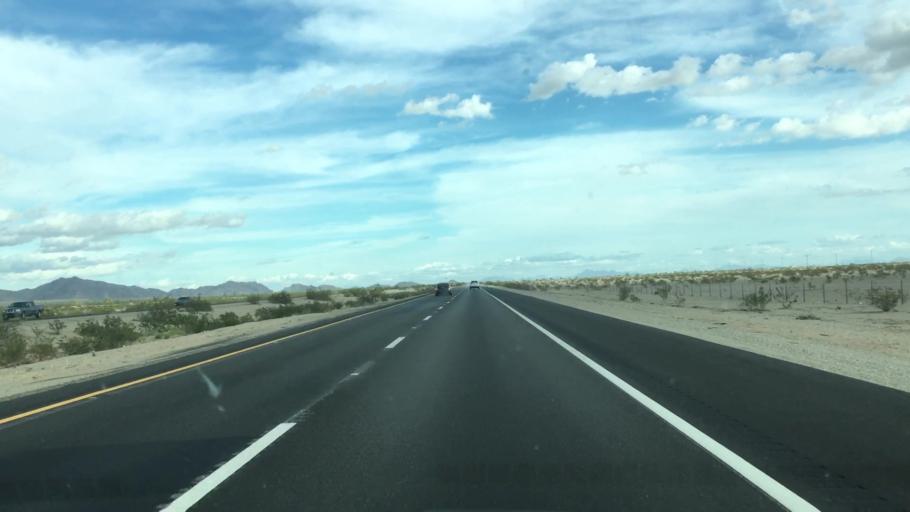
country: US
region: California
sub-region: Riverside County
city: Mesa Verde
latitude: 33.6084
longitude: -114.8763
